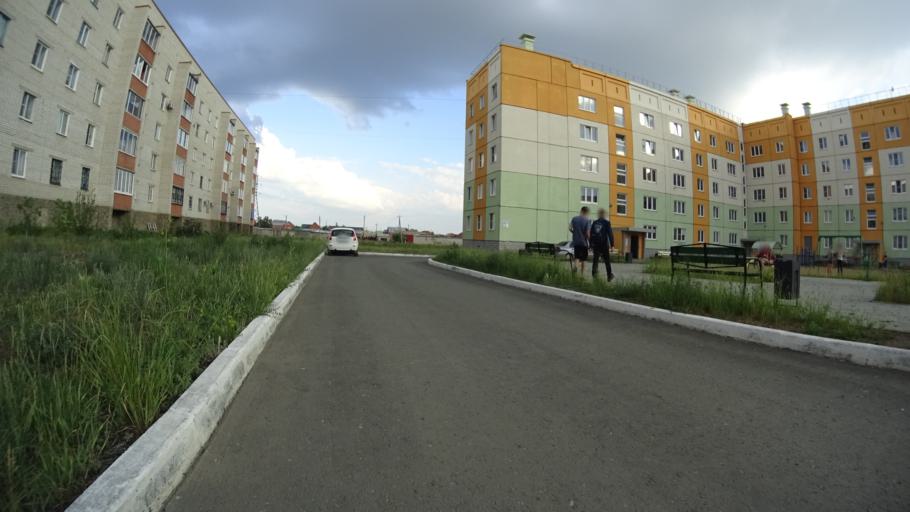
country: RU
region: Chelyabinsk
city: Troitsk
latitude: 54.0720
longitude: 61.5323
